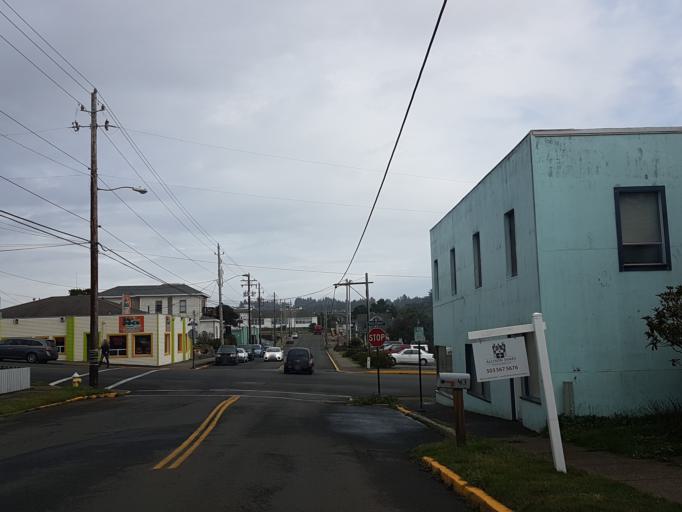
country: US
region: Oregon
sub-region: Lincoln County
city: Newport
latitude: 44.6323
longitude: -124.0565
